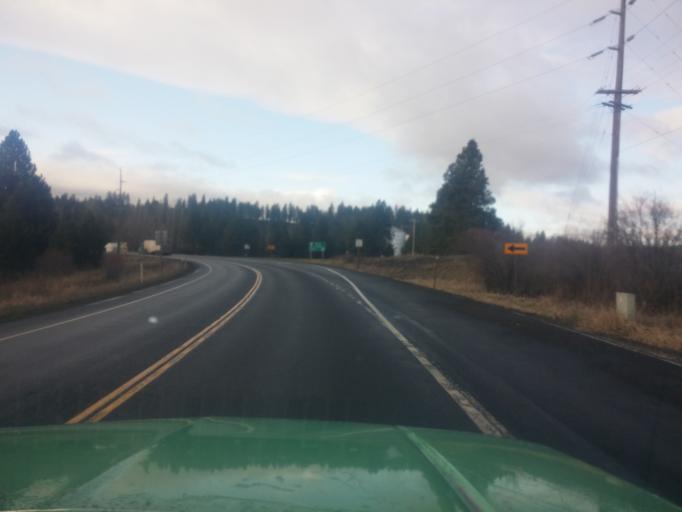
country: US
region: Idaho
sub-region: Latah County
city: Moscow
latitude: 46.9202
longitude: -116.9505
